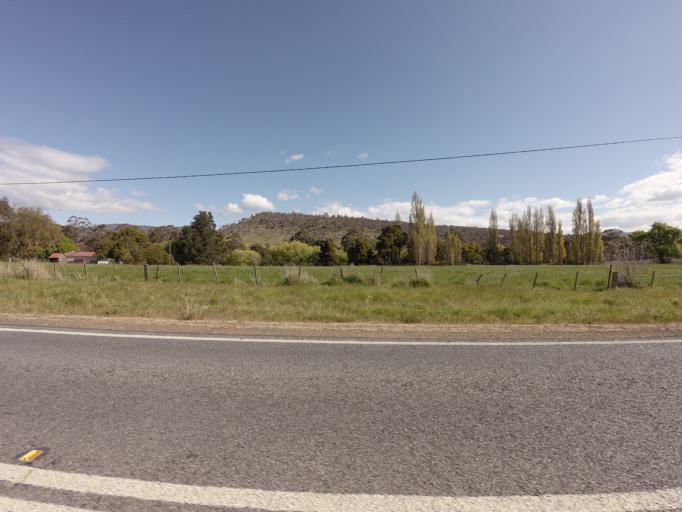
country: AU
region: Tasmania
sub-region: Derwent Valley
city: New Norfolk
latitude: -42.7620
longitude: 147.0132
